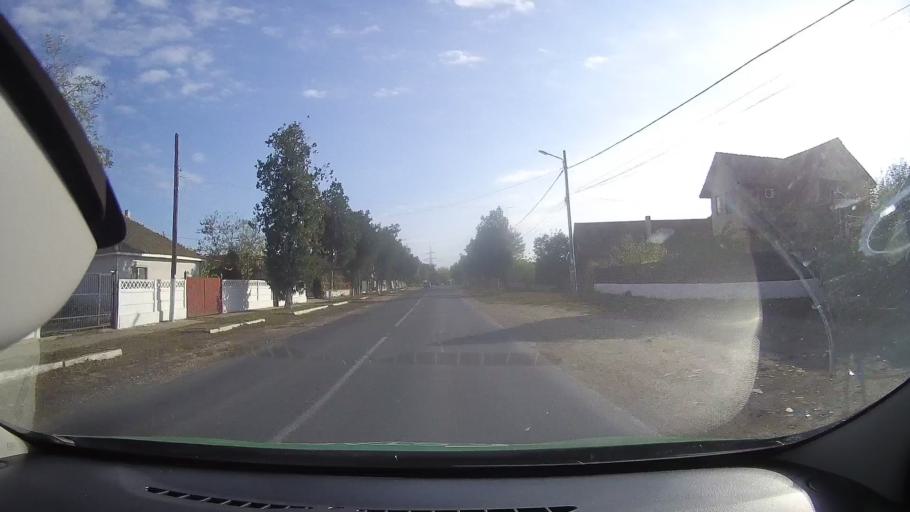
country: RO
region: Constanta
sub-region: Comuna Corbu
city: Corbu
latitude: 44.3790
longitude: 28.6628
